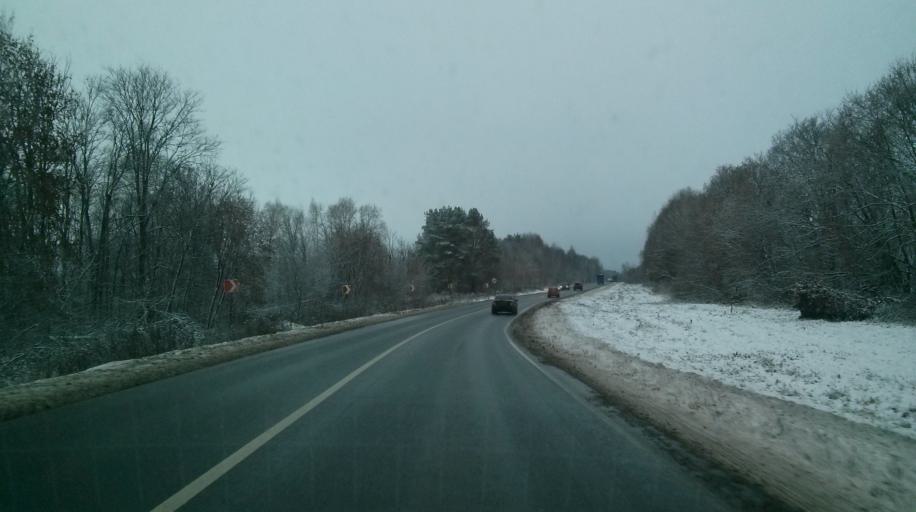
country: RU
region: Nizjnij Novgorod
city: Bogorodsk
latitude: 56.0519
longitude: 43.4047
